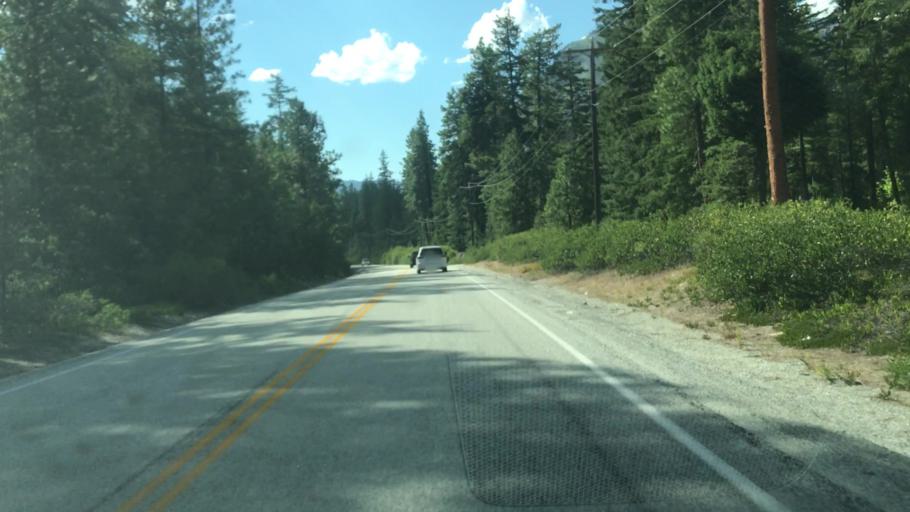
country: US
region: Washington
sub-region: Chelan County
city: Leavenworth
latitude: 47.8235
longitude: -120.7524
